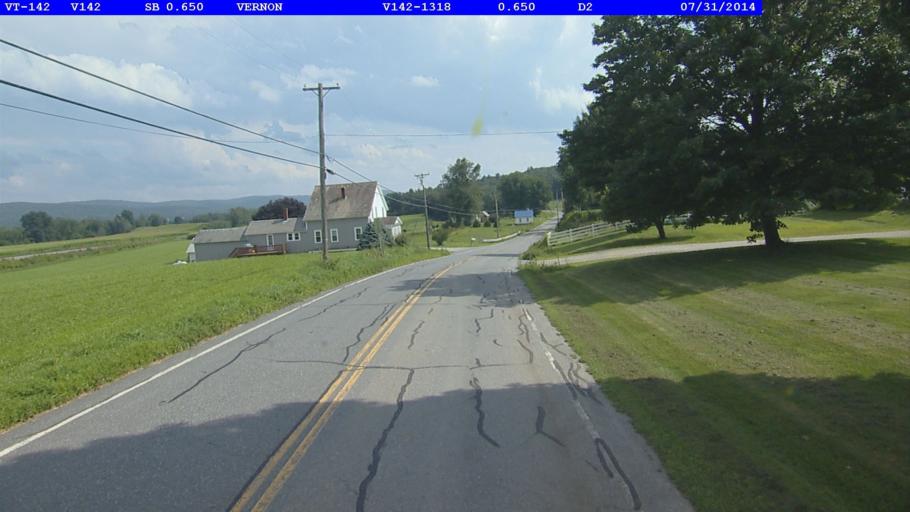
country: US
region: Massachusetts
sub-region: Franklin County
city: Northfield
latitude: 42.7356
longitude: -72.4692
